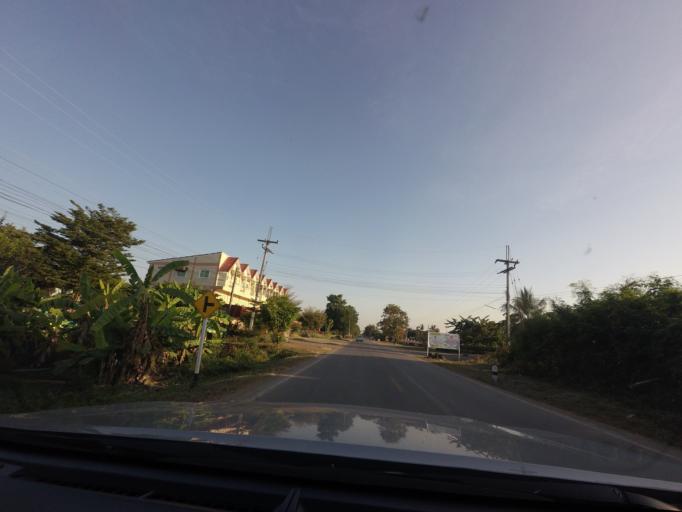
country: TH
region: Sukhothai
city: Sawankhalok
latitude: 17.3835
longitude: 99.7926
